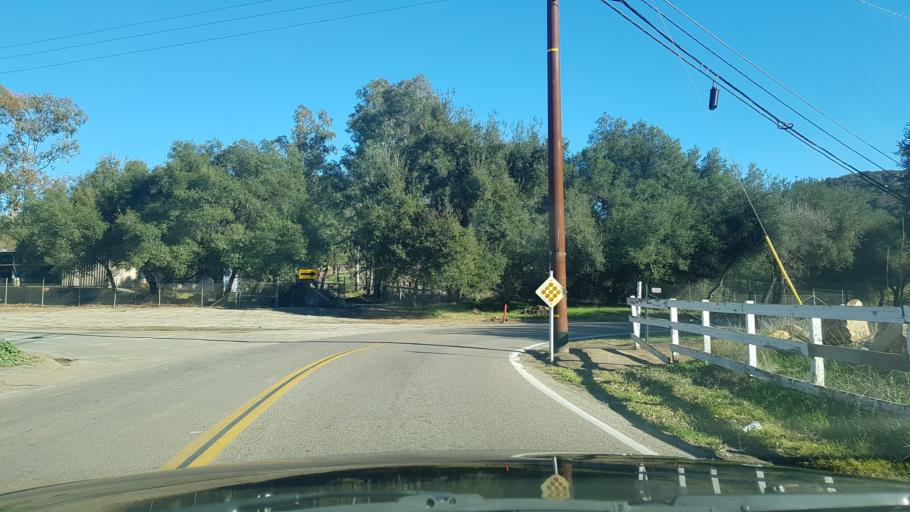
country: US
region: California
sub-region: San Diego County
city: Valley Center
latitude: 33.2019
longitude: -116.9672
